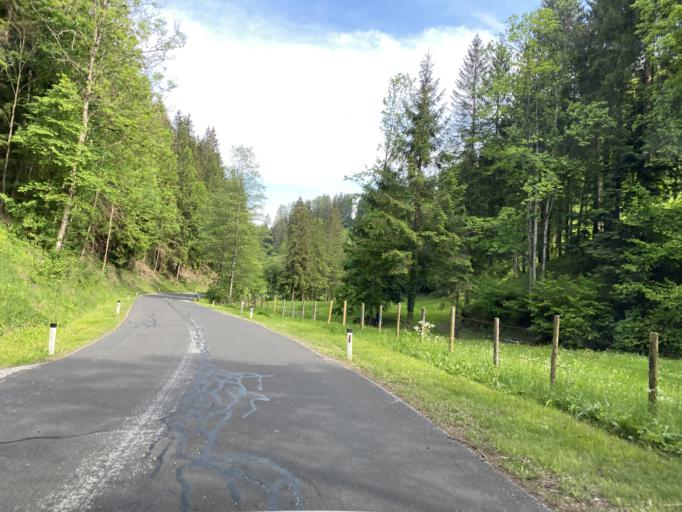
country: AT
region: Styria
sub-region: Politischer Bezirk Weiz
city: Koglhof
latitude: 47.3063
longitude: 15.6627
